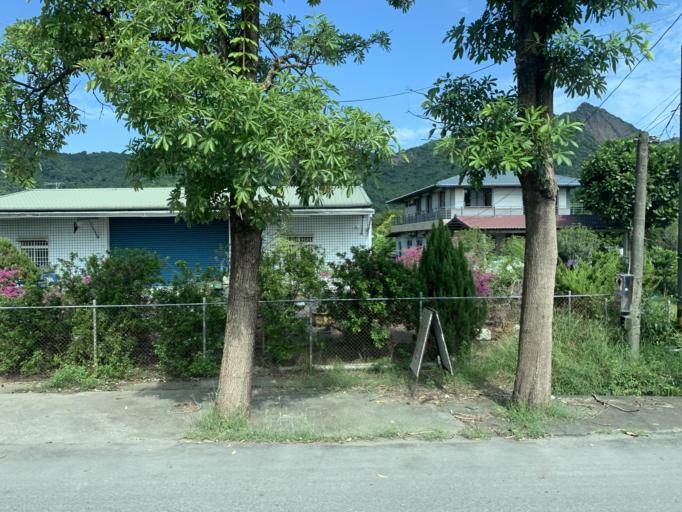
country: TW
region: Taiwan
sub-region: Pingtung
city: Pingtung
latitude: 22.8924
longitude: 120.5112
